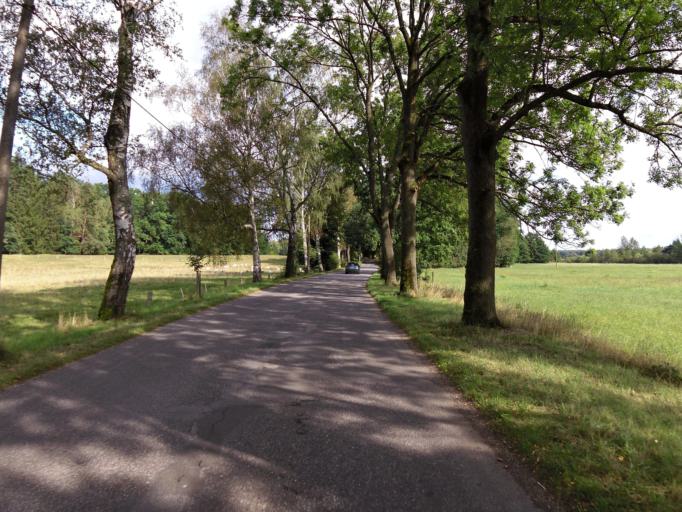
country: CZ
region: Jihocesky
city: Suchdol nad Luznici
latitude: 48.9048
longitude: 14.8900
